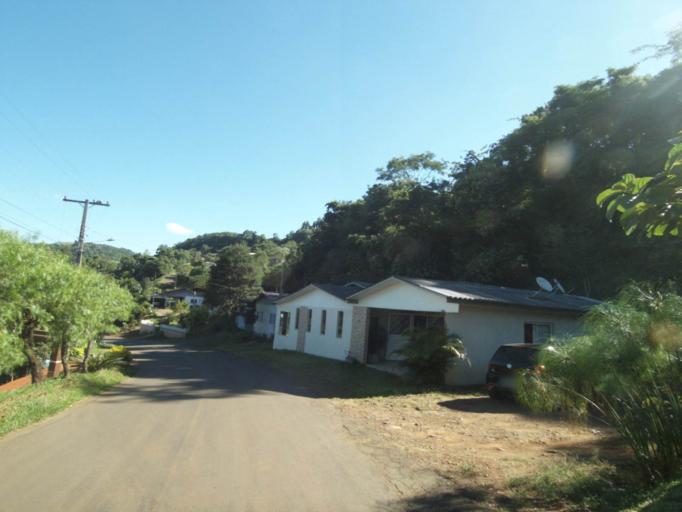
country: BR
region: Parana
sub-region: Ampere
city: Ampere
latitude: -26.1704
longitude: -53.3660
